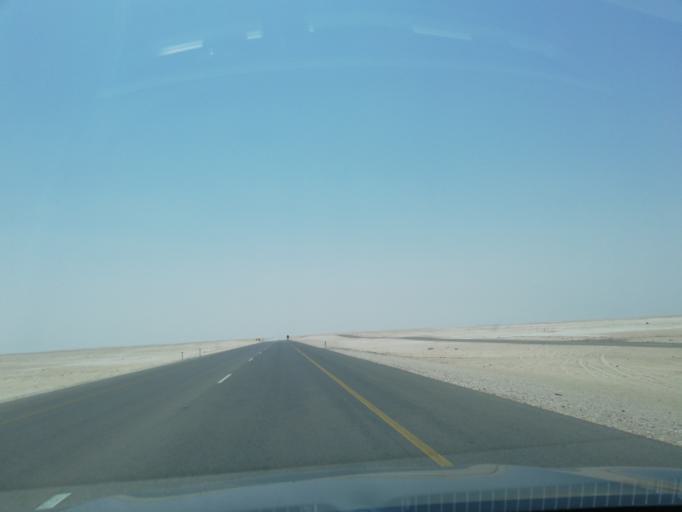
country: OM
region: Al Wusta
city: Hayma'
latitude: 19.7064
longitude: 55.9863
